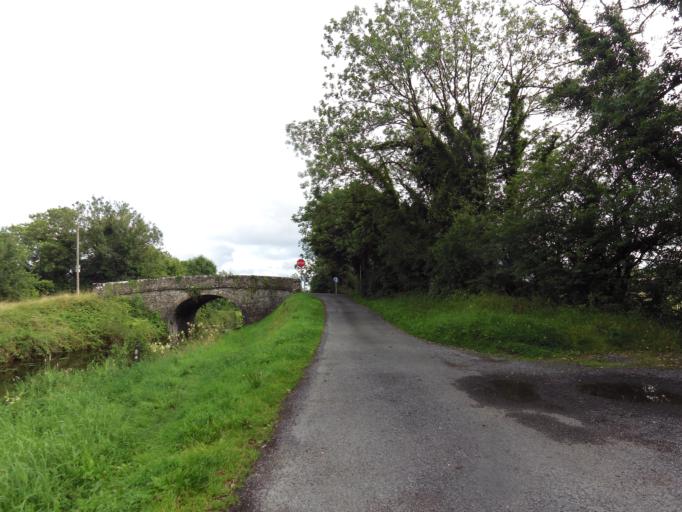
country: IE
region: Leinster
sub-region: An Iarmhi
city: An Muileann gCearr
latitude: 53.5571
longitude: -7.4833
